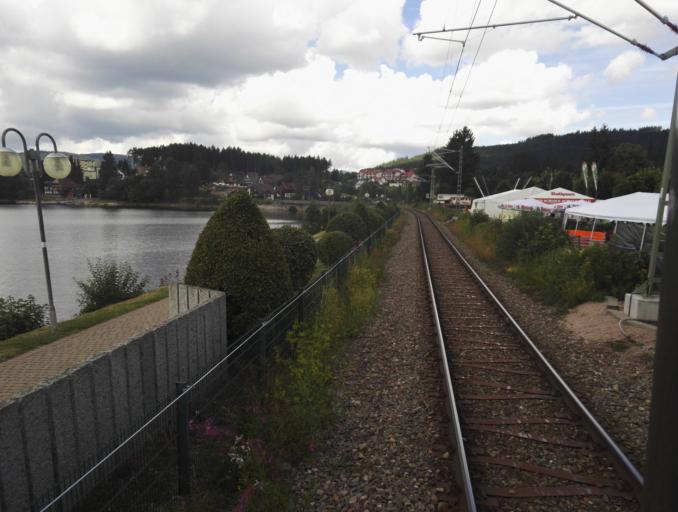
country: DE
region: Baden-Wuerttemberg
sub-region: Freiburg Region
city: Schluchsee
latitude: 47.8174
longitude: 8.1758
